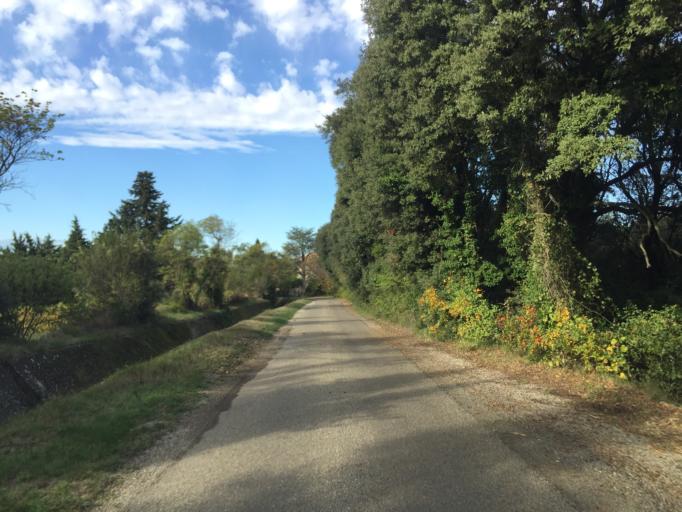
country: FR
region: Provence-Alpes-Cote d'Azur
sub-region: Departement du Vaucluse
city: Orange
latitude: 44.1178
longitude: 4.8036
